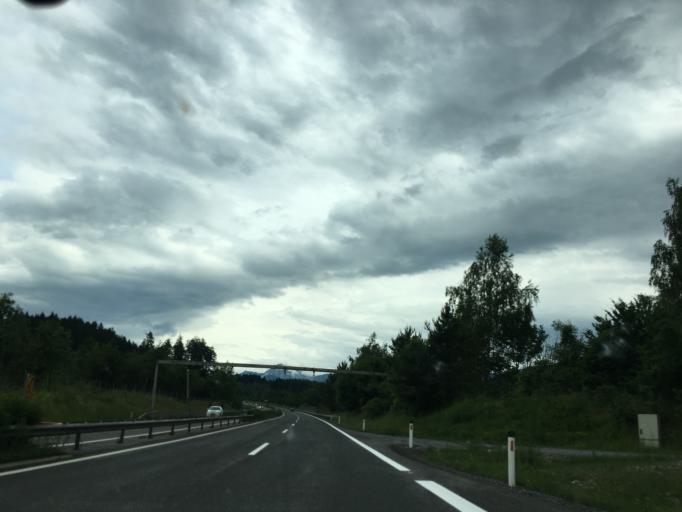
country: AT
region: Carinthia
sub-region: Politischer Bezirk Villach Land
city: Rosegg
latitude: 46.5851
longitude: 13.9874
